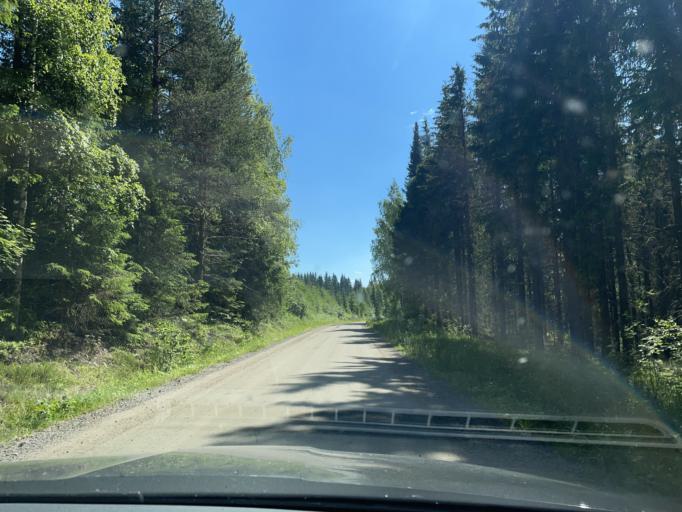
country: FI
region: Central Finland
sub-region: Saarijaervi-Viitasaari
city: Viitasaari
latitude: 63.2369
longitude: 25.9528
